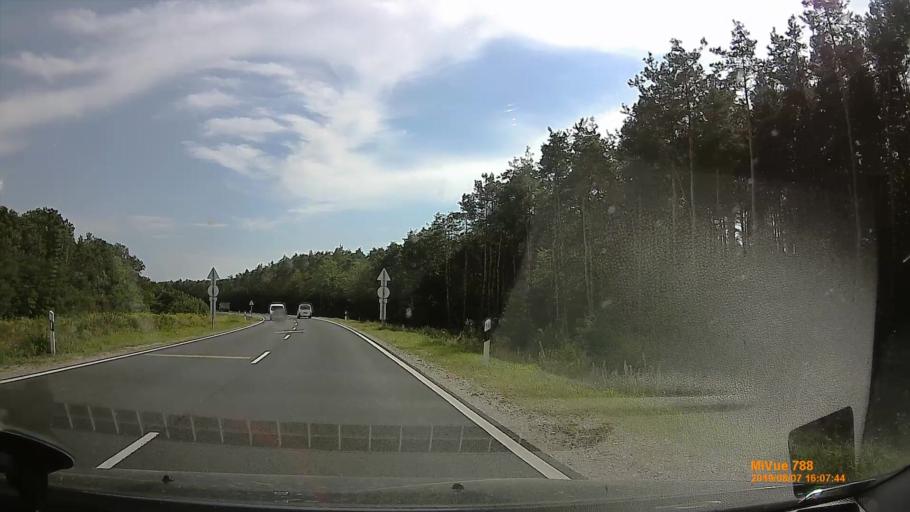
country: HU
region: Zala
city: Zalalovo
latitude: 46.9179
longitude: 16.5987
